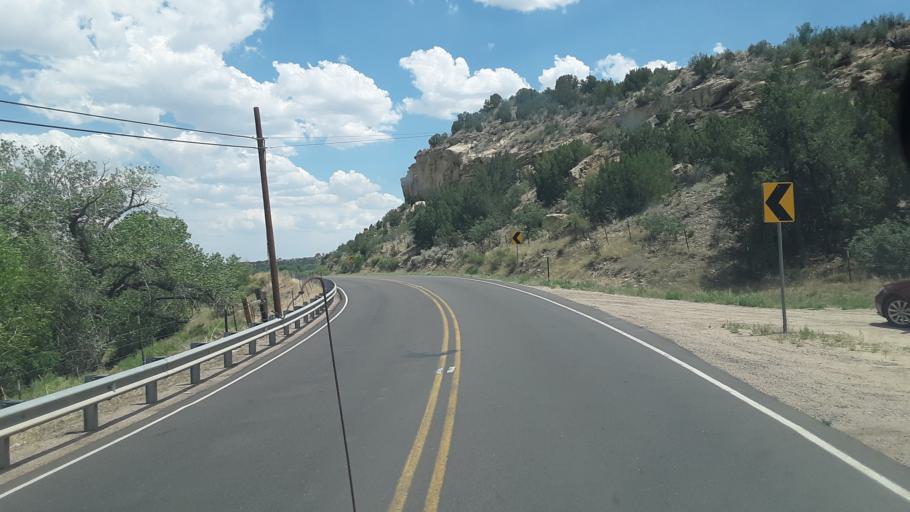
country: US
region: Colorado
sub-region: Fremont County
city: Lincoln Park
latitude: 38.4151
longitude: -105.1803
